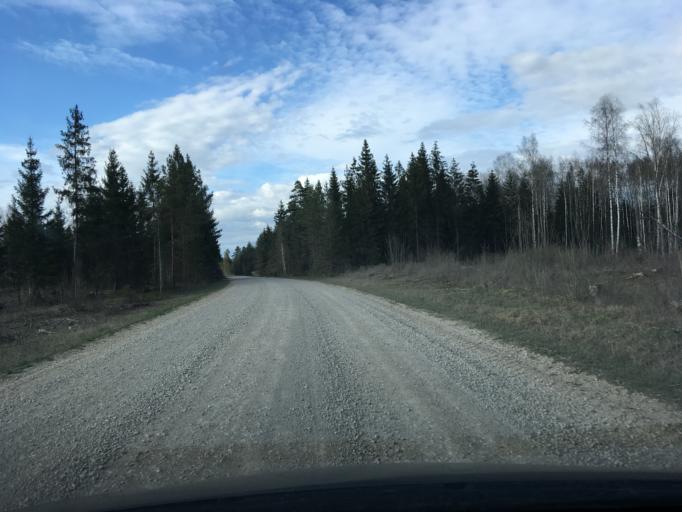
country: EE
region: Raplamaa
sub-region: Maerjamaa vald
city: Marjamaa
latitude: 58.9613
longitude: 24.3299
